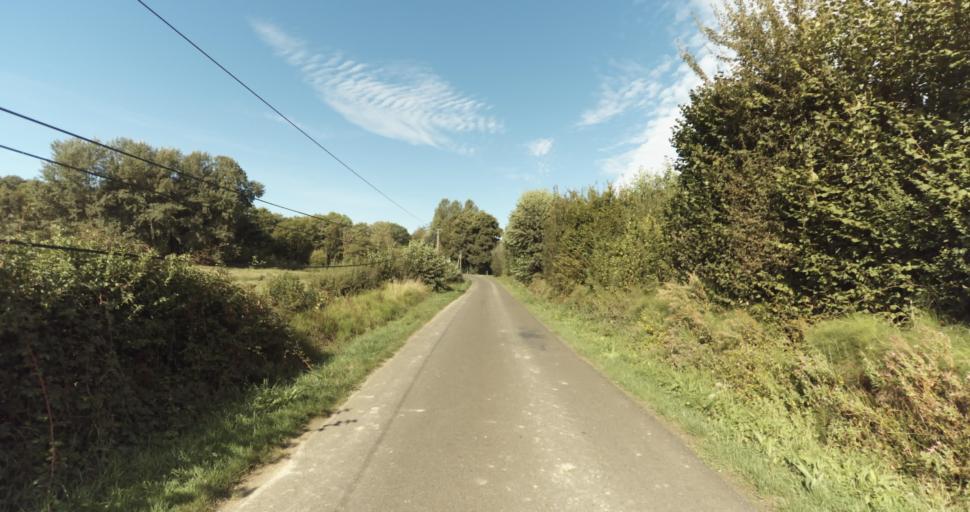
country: FR
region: Lower Normandy
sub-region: Departement de l'Orne
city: Gace
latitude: 48.8140
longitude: 0.2165
